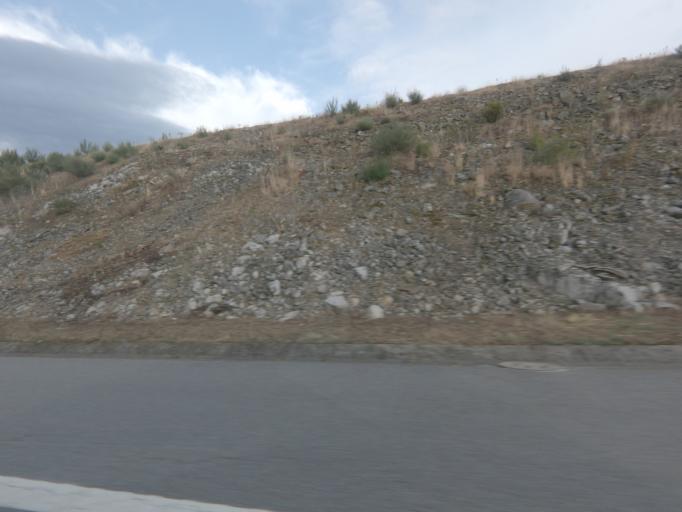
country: PT
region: Viseu
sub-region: Castro Daire
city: Castro Daire
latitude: 40.9780
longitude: -7.8844
